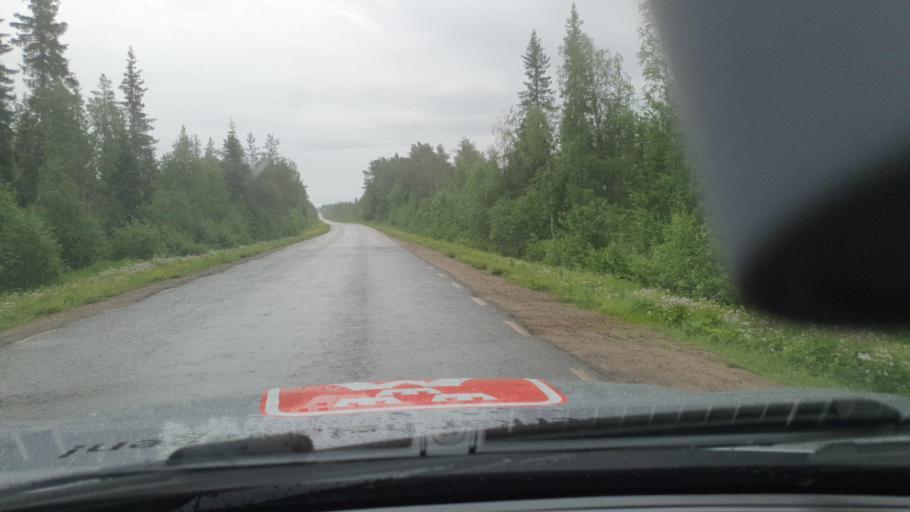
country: SE
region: Norrbotten
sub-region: Pajala Kommun
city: Pajala
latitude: 66.8397
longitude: 23.0819
